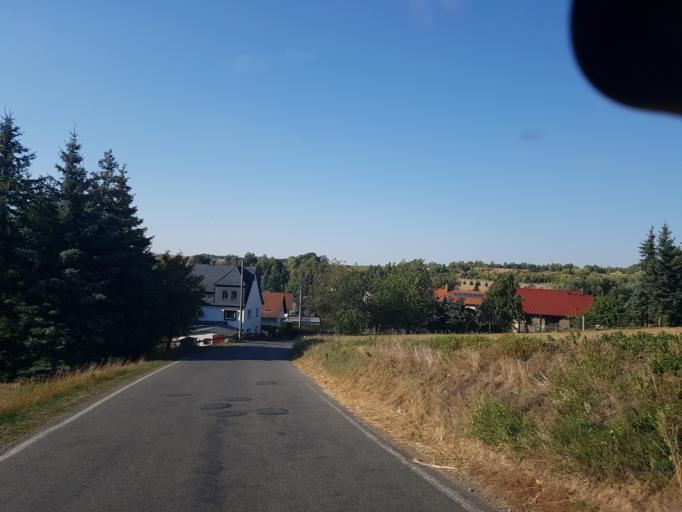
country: DE
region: Saxony
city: Dobeln
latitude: 51.1781
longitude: 13.1134
